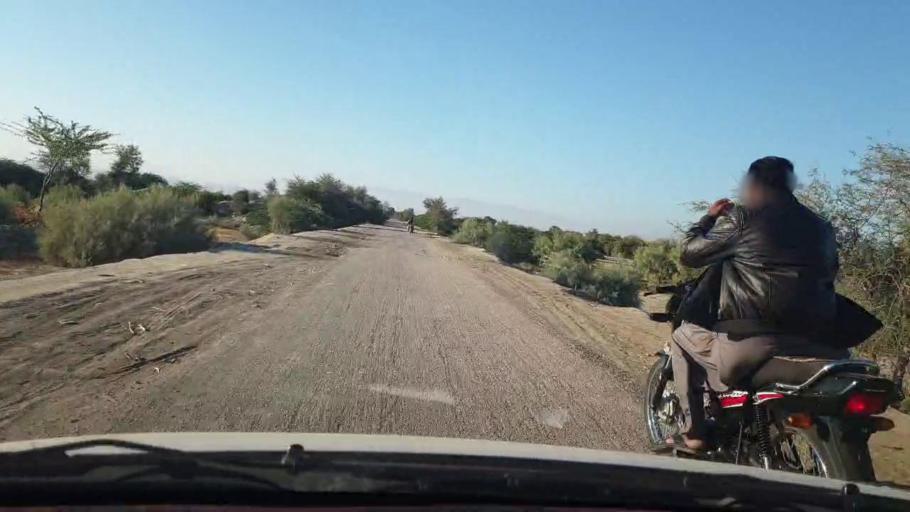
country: PK
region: Sindh
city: Johi
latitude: 26.7713
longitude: 67.4575
